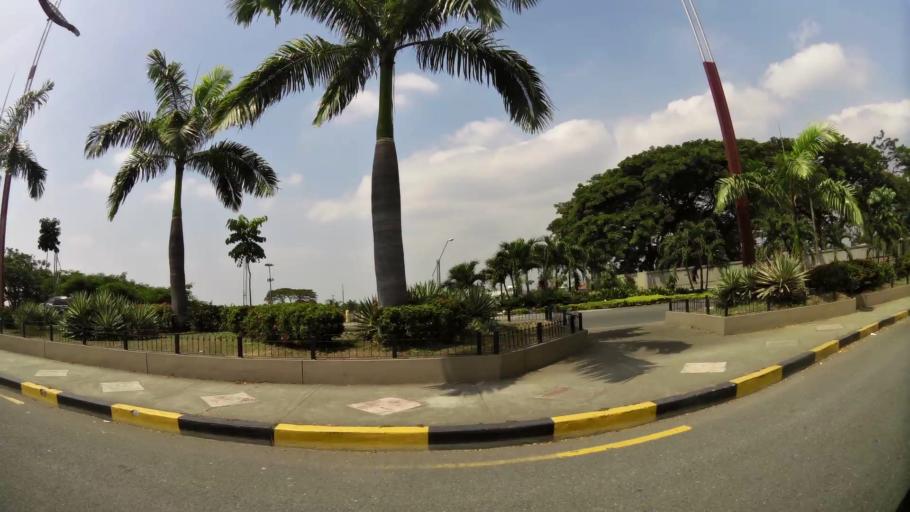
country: EC
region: Guayas
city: Eloy Alfaro
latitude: -2.1536
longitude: -79.8656
